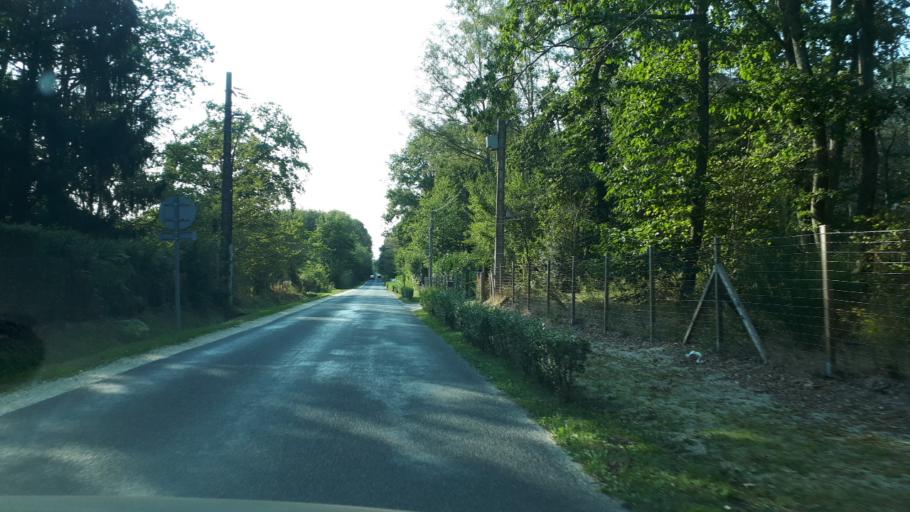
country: FR
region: Centre
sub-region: Departement du Cher
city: Saint-Eloy-de-Gy
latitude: 47.2255
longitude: 2.3119
